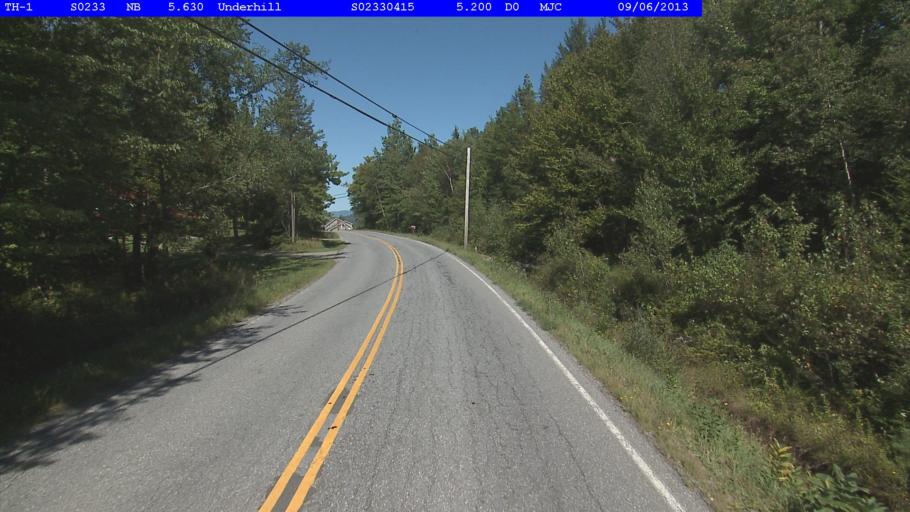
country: US
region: Vermont
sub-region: Chittenden County
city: Jericho
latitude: 44.5402
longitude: -72.8703
